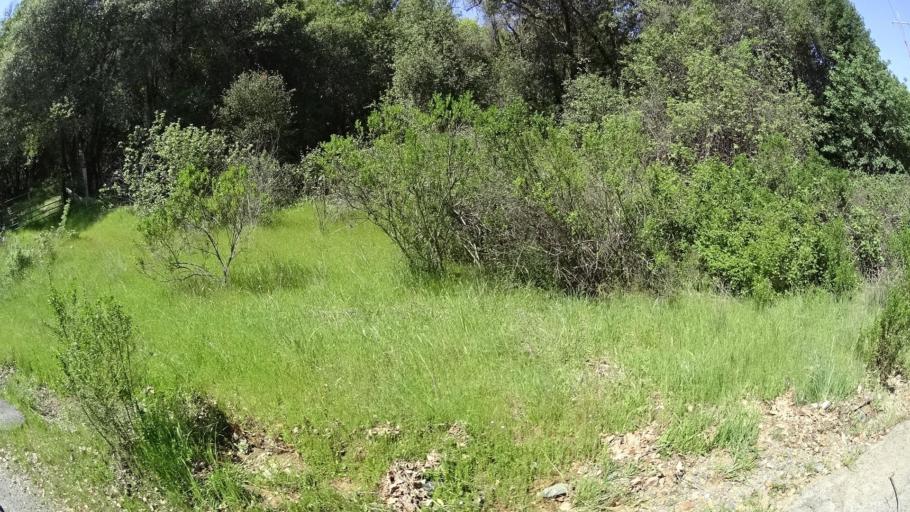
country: US
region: California
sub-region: Humboldt County
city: Redway
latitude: 40.1642
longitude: -123.6033
